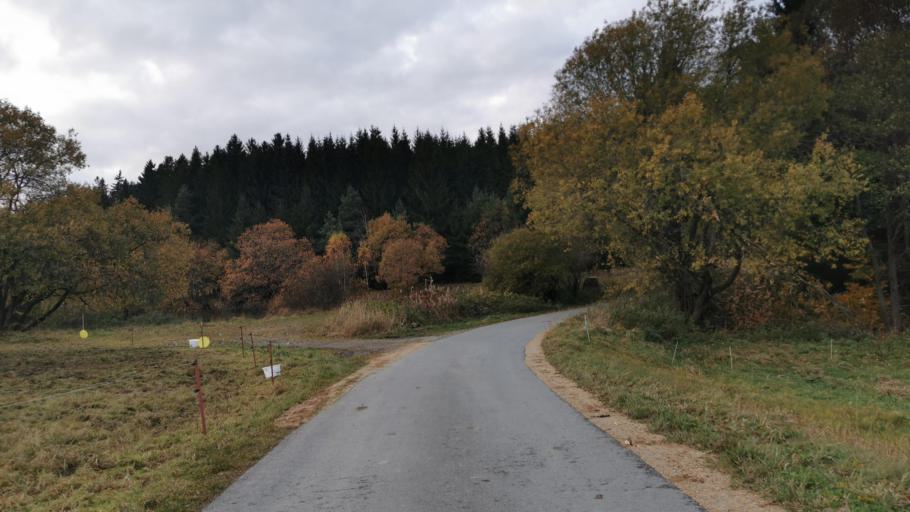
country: DE
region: Thuringia
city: Wurzbach
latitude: 50.4736
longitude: 11.5063
